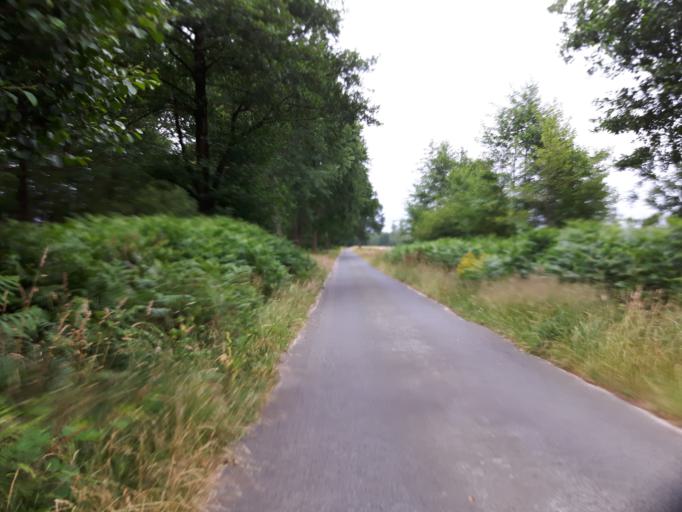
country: DE
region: Lower Saxony
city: Garstedt
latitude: 53.2744
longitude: 10.1860
